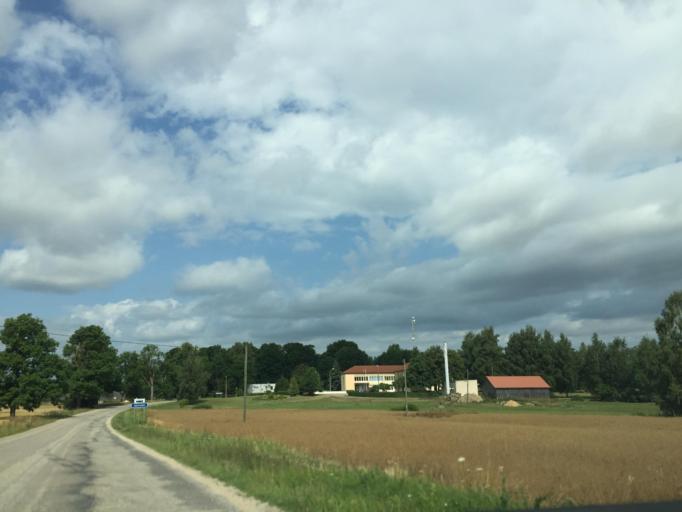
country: LV
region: Kandava
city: Kandava
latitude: 56.9707
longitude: 22.9330
